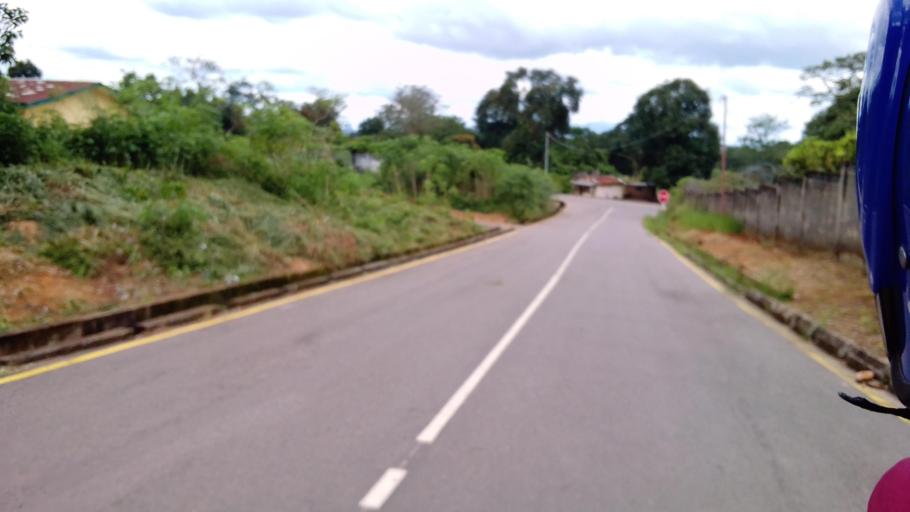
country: SL
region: Eastern Province
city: Koidu
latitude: 8.6553
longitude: -10.9857
